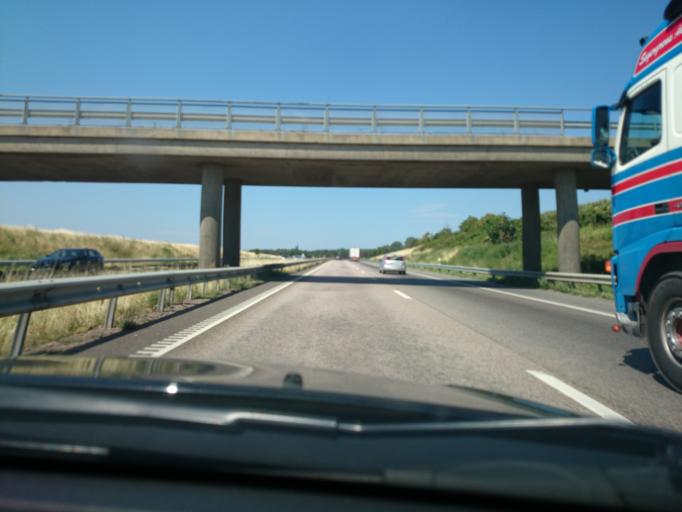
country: SE
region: Skane
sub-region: Kavlinge Kommun
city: Loddekopinge
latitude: 55.7518
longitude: 13.0081
